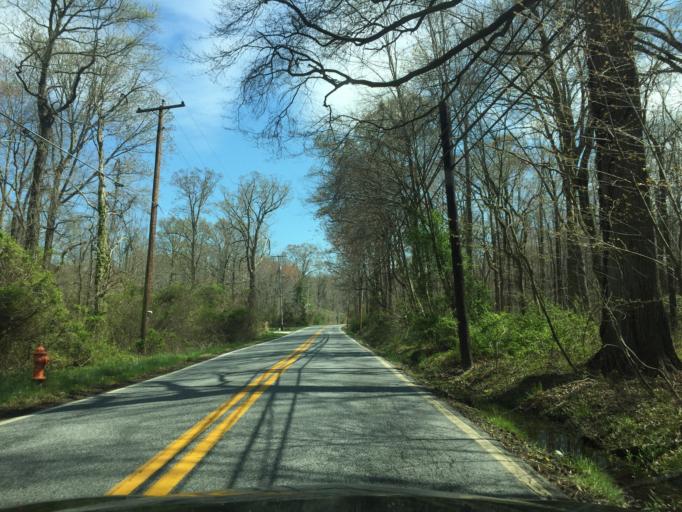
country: US
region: Maryland
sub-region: Baltimore County
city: Edgemere
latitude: 39.2622
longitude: -76.4189
